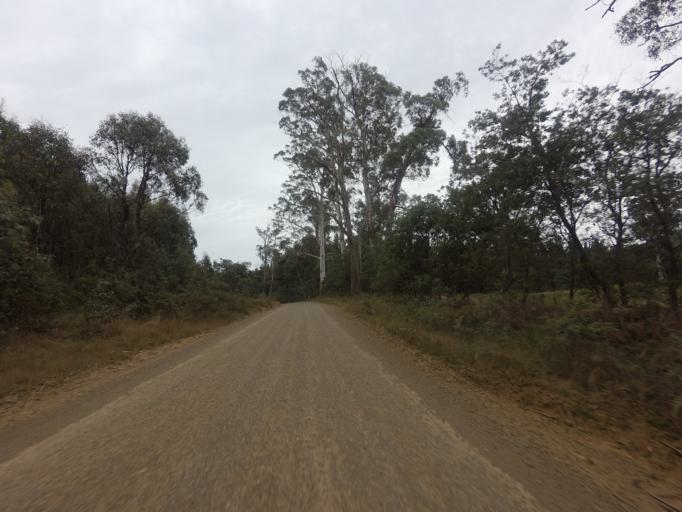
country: AU
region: Tasmania
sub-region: Derwent Valley
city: New Norfolk
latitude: -42.5765
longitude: 147.0013
